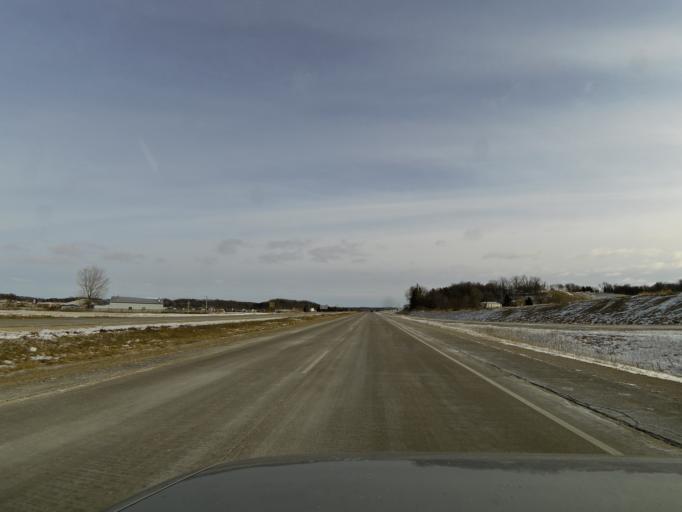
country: US
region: Wisconsin
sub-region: Pierce County
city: River Falls
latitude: 44.8972
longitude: -92.6465
